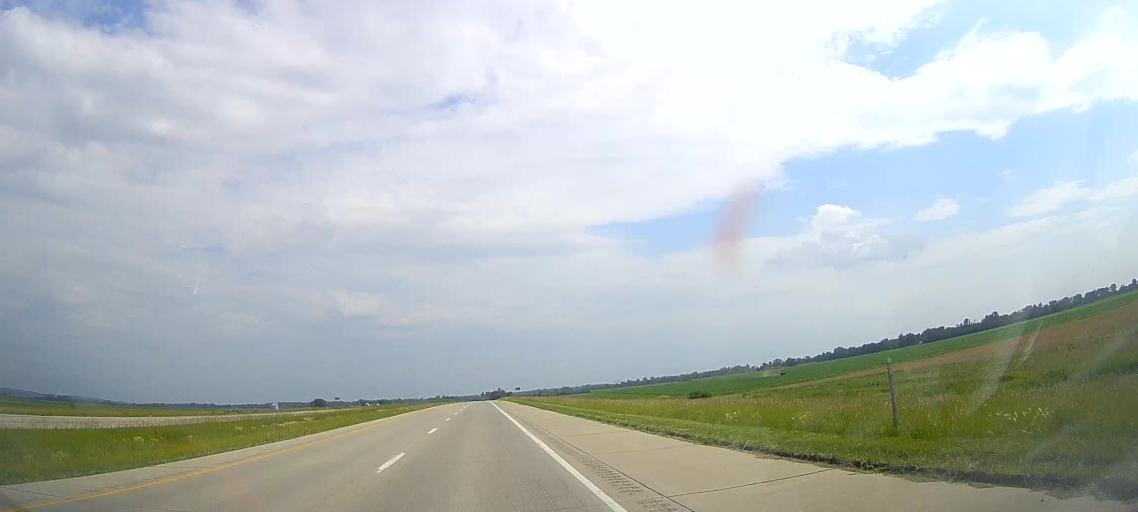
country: US
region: Nebraska
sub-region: Burt County
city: Tekamah
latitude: 41.8667
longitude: -96.1035
